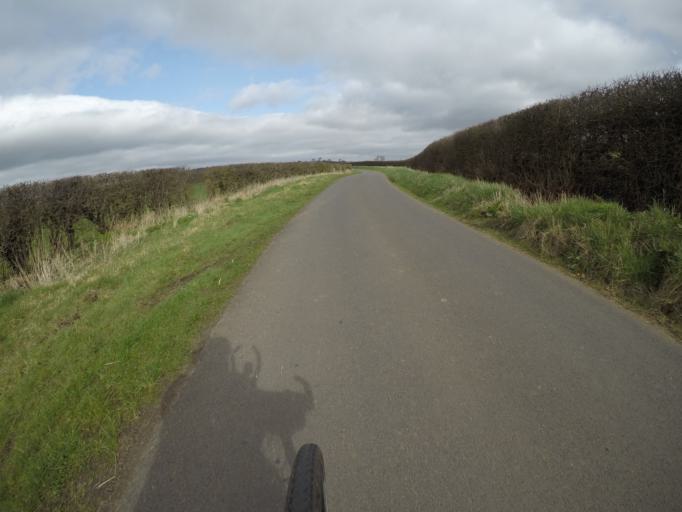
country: GB
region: Scotland
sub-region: North Ayrshire
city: Irvine
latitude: 55.6396
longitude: -4.6298
